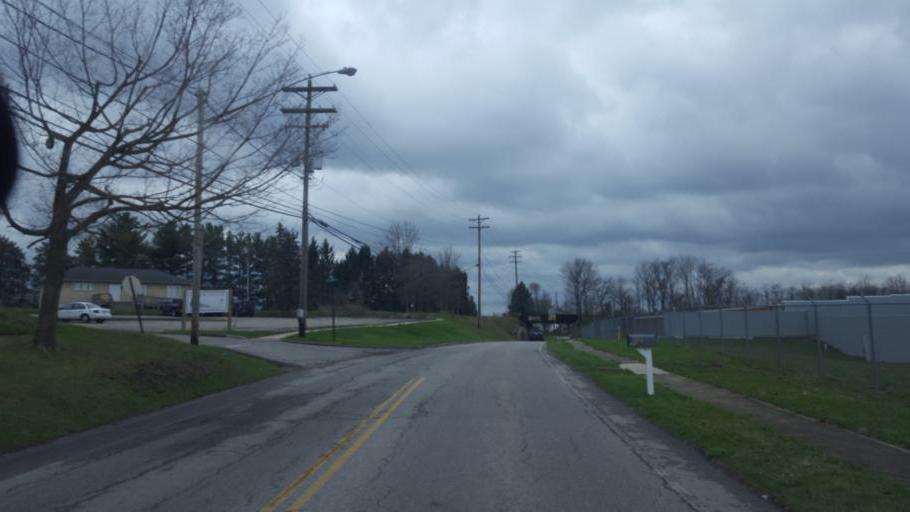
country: US
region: Ohio
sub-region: Delaware County
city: Sunbury
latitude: 40.2397
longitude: -82.8601
